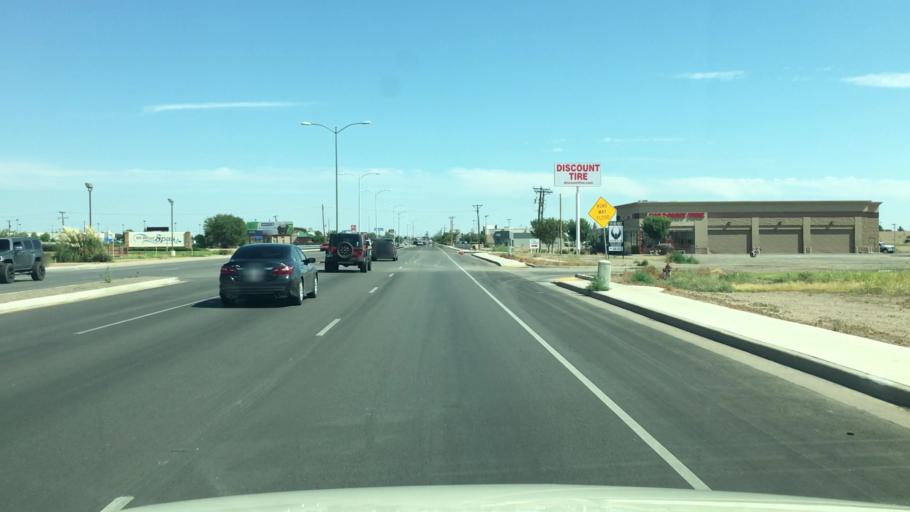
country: US
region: New Mexico
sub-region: Chaves County
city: Roswell
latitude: 33.4433
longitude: -104.5232
